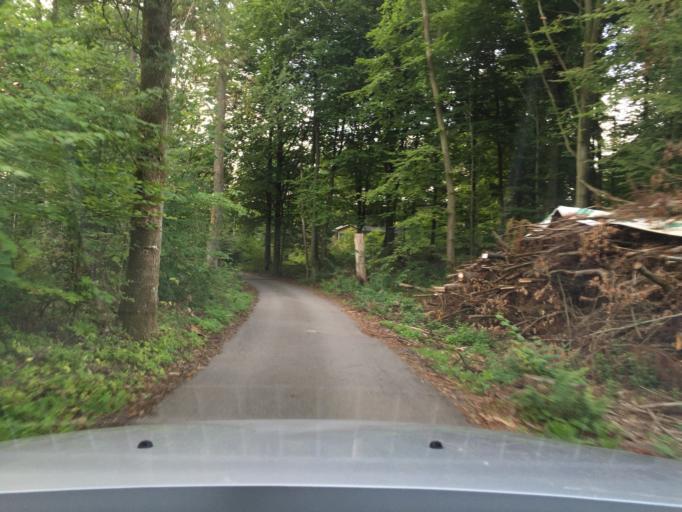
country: SE
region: Skane
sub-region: Hassleholms Kommun
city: Sosdala
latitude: 56.0004
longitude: 13.6376
